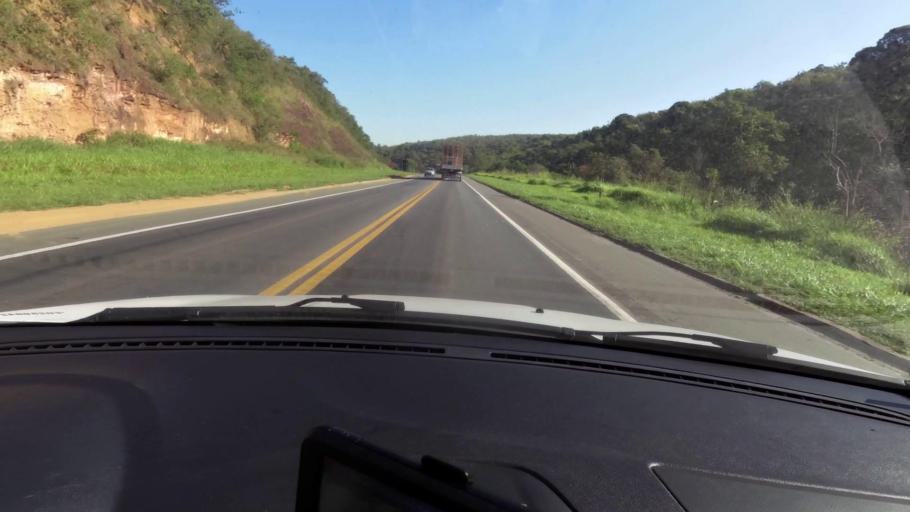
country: BR
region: Espirito Santo
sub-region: Alfredo Chaves
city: Alfredo Chaves
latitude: -20.6769
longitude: -40.6658
